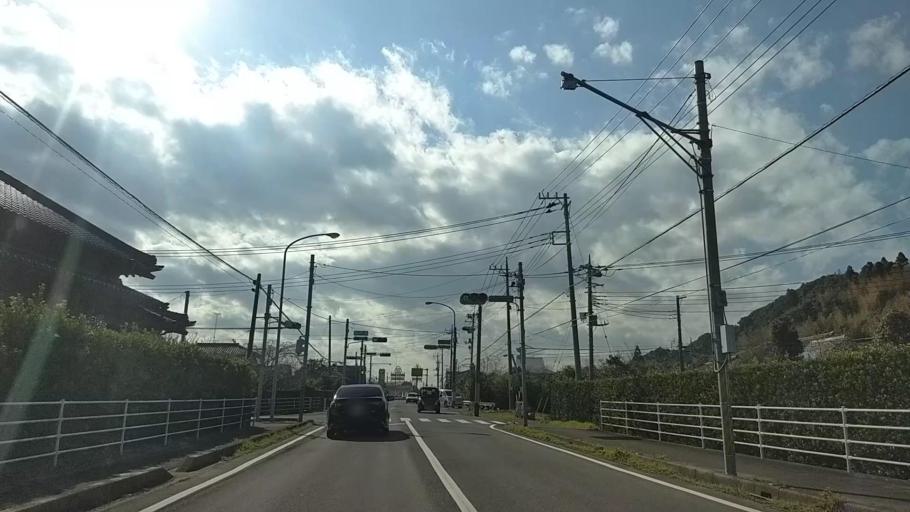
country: JP
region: Chiba
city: Naruto
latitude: 35.6228
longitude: 140.4393
